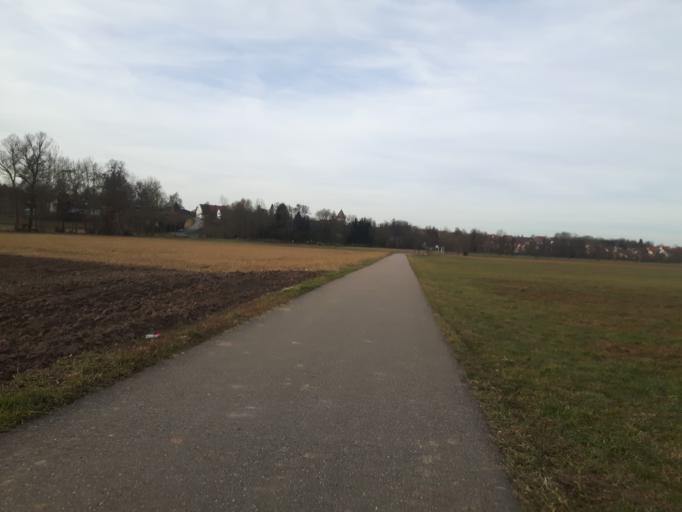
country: DE
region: Baden-Wuerttemberg
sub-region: Regierungsbezirk Stuttgart
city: Bretzfeld
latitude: 49.1690
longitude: 9.4350
